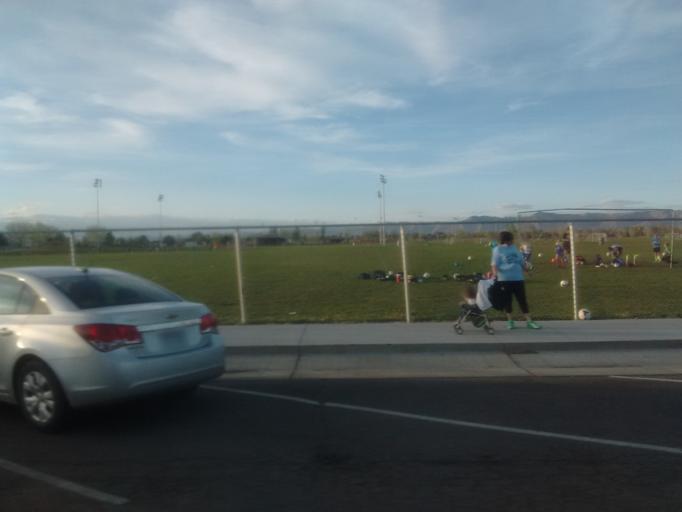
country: US
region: Colorado
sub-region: Mesa County
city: Redlands
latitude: 39.1063
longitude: -108.6060
